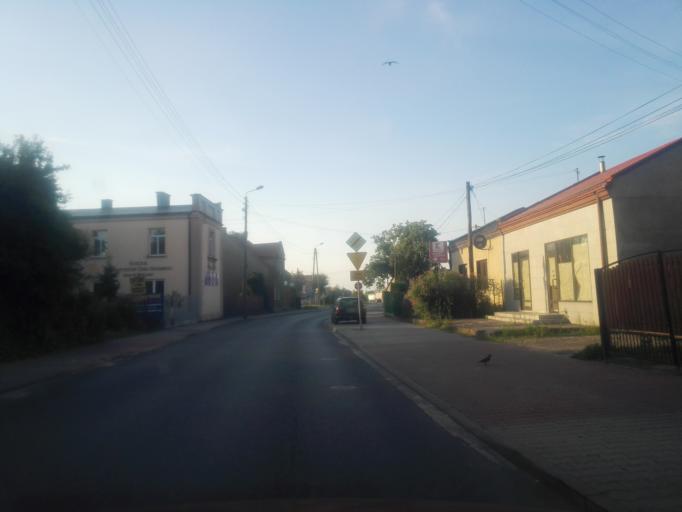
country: PL
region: Lodz Voivodeship
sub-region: Powiat wielunski
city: Wielun
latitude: 51.2223
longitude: 18.5742
